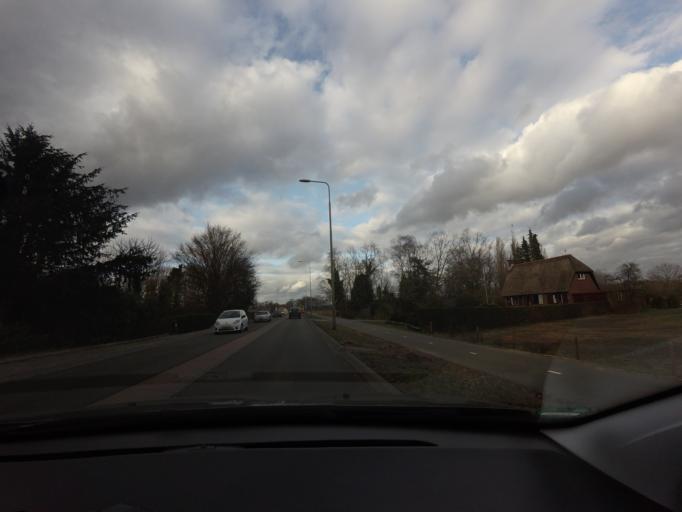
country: NL
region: Gelderland
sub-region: Gemeente Lochem
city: Gorssel
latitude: 52.2092
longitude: 6.1968
